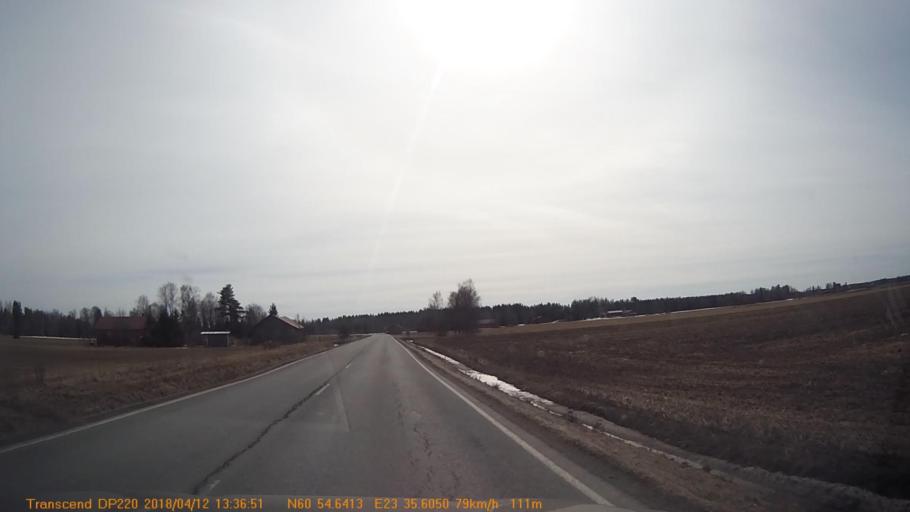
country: FI
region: Haeme
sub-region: Forssa
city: Forssa
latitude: 60.9103
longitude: 23.5933
